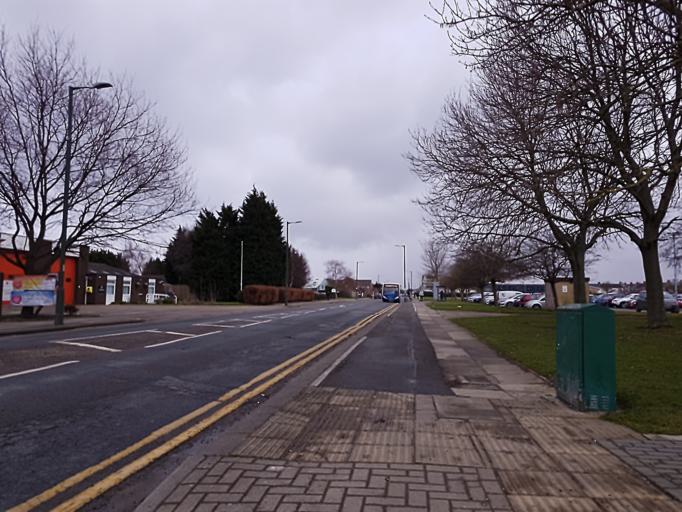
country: GB
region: England
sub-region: North East Lincolnshire
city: Grimbsy
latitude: 53.5694
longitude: -0.1129
